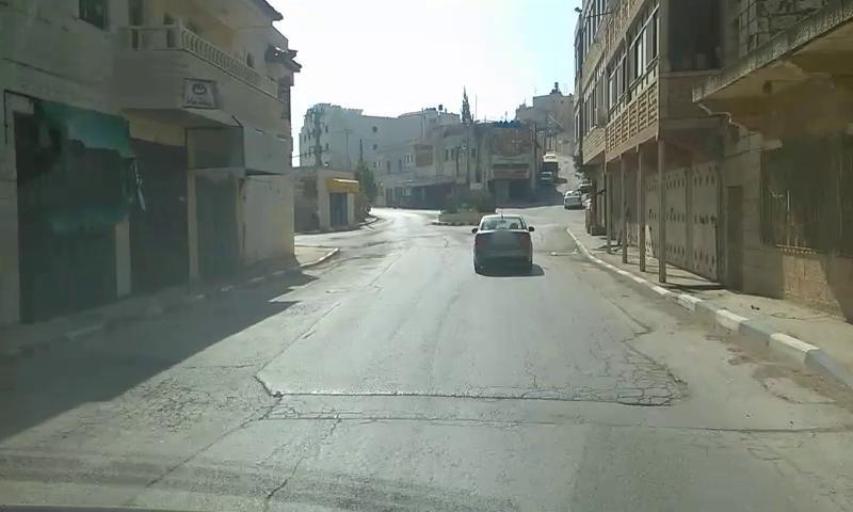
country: PS
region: West Bank
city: At Taybah
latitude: 31.9563
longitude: 35.2986
